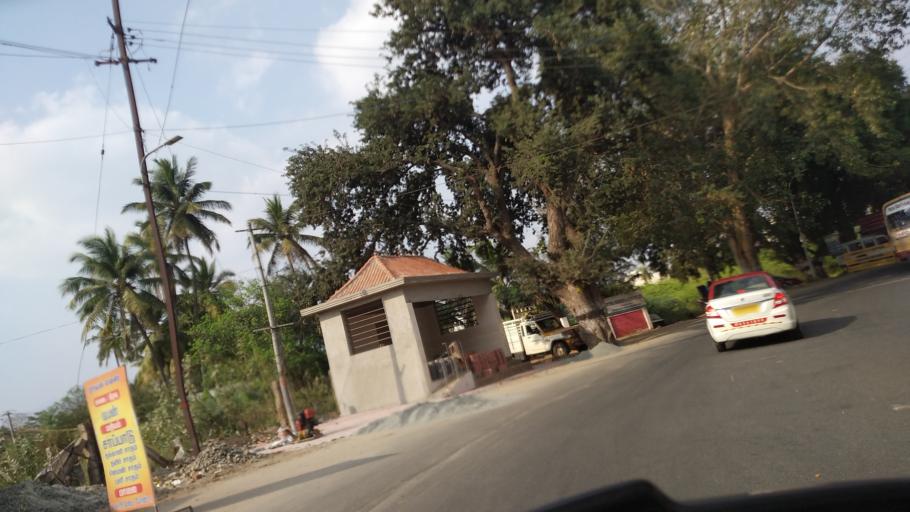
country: IN
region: Tamil Nadu
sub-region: Coimbatore
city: Perur
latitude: 10.9826
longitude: 76.9214
